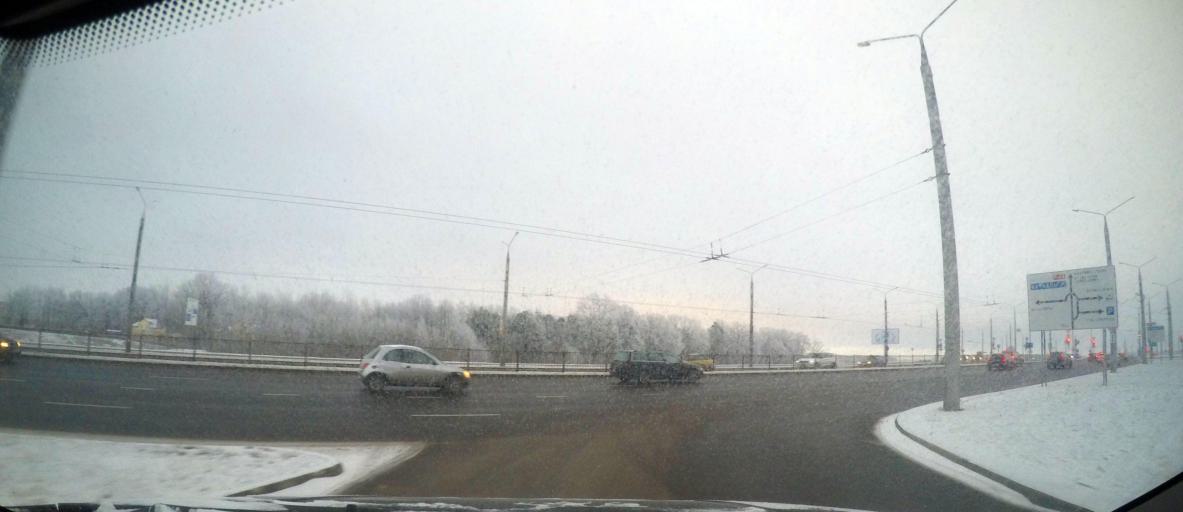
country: BY
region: Grodnenskaya
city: Hrodna
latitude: 53.6509
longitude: 23.8568
